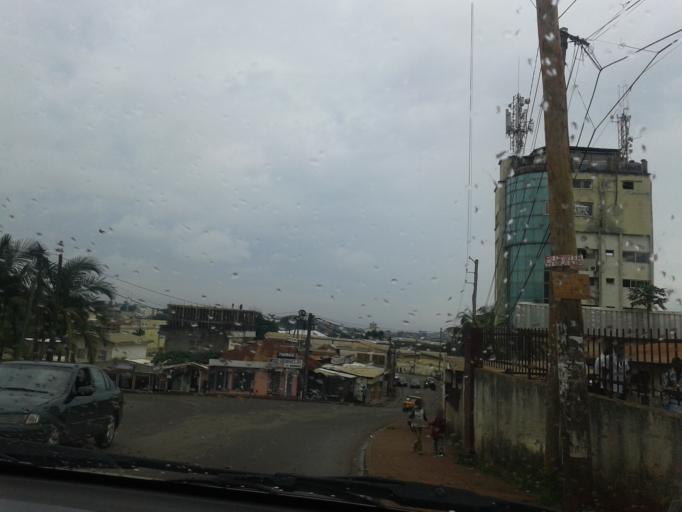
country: CM
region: Centre
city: Yaounde
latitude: 3.8890
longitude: 11.5170
